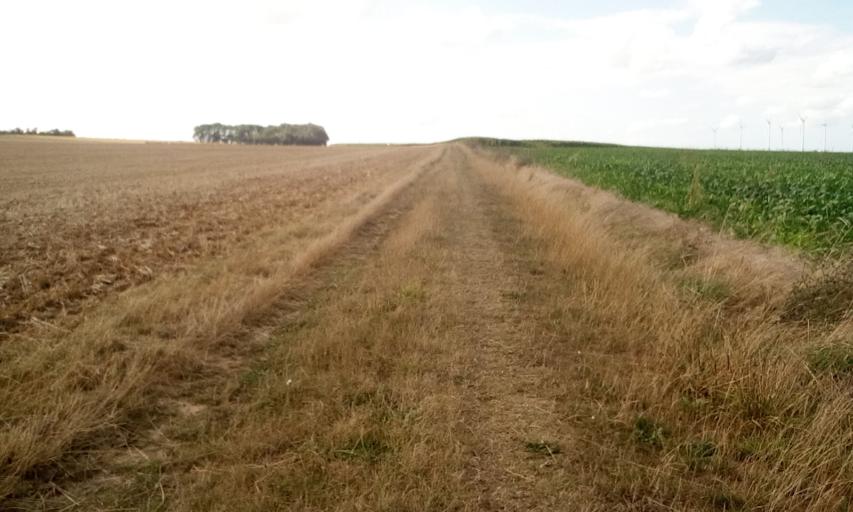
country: FR
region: Lower Normandy
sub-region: Departement du Calvados
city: Saint-Sylvain
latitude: 49.0704
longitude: -0.2413
